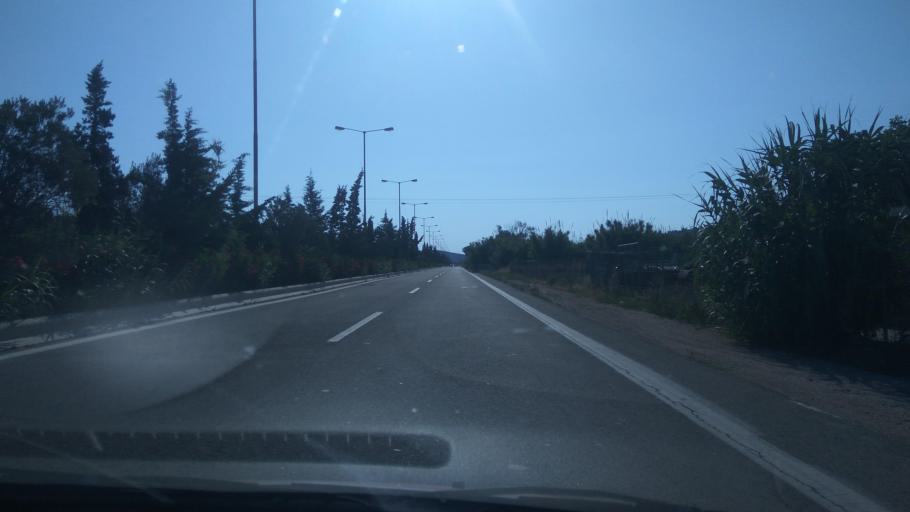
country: GR
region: Attica
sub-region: Nomarchia Anatolikis Attikis
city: Keratea
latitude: 37.8020
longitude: 24.0196
